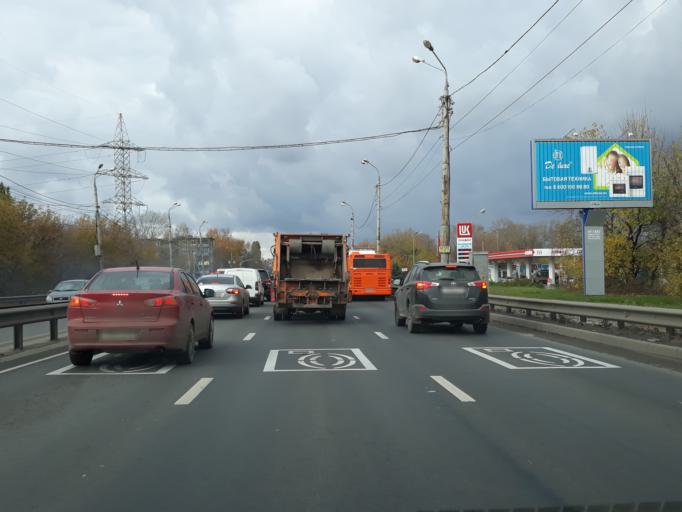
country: RU
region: Nizjnij Novgorod
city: Nizhniy Novgorod
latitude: 56.2572
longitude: 43.9348
